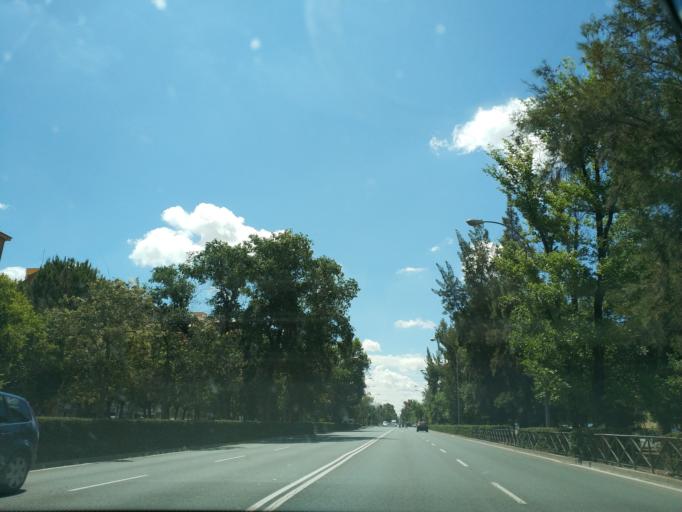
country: ES
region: Andalusia
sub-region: Provincia de Sevilla
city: Sevilla
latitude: 37.3682
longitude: -5.9677
